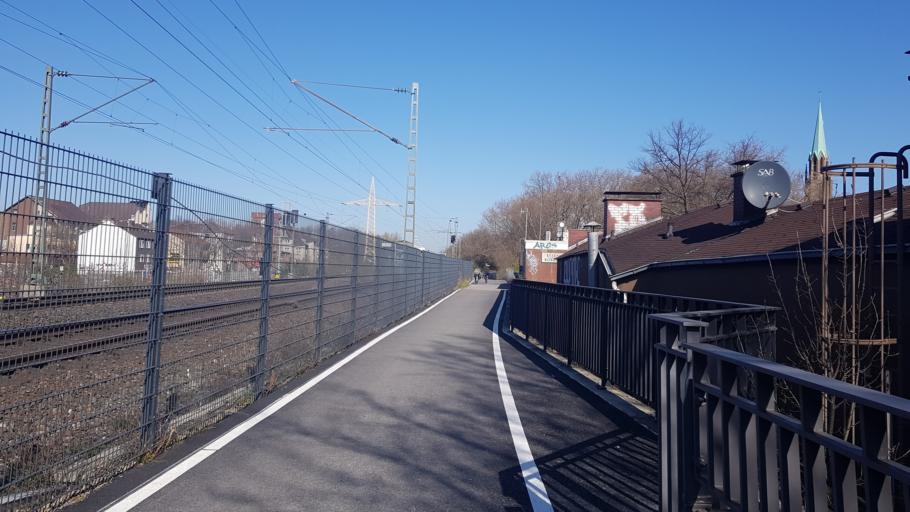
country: DE
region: North Rhine-Westphalia
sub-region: Regierungsbezirk Munster
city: Bottrop
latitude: 51.4719
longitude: 6.9496
